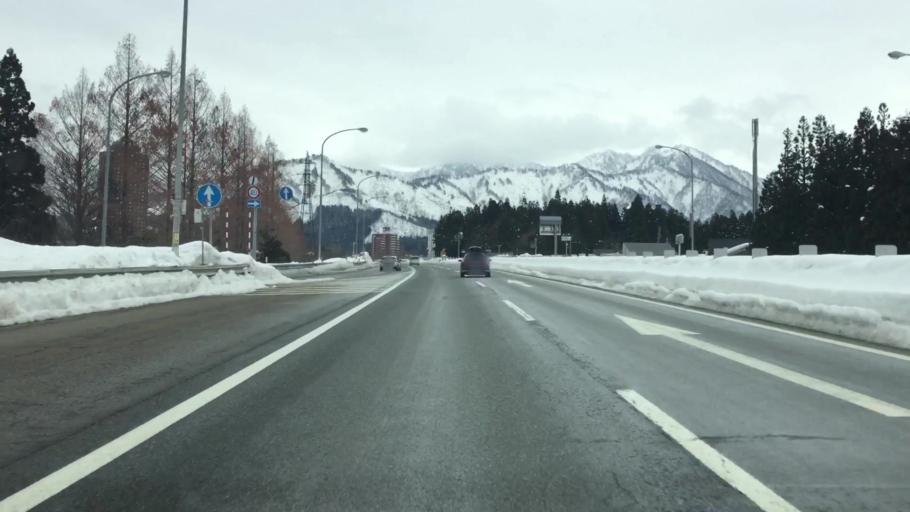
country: JP
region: Niigata
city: Shiozawa
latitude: 36.9323
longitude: 138.8296
